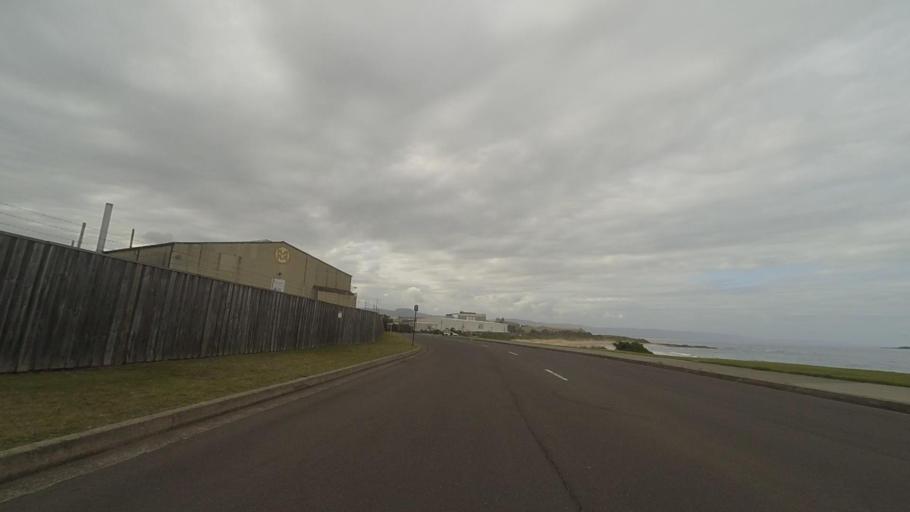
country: AU
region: New South Wales
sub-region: Wollongong
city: Port Kembla
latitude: -34.4842
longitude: 150.9143
